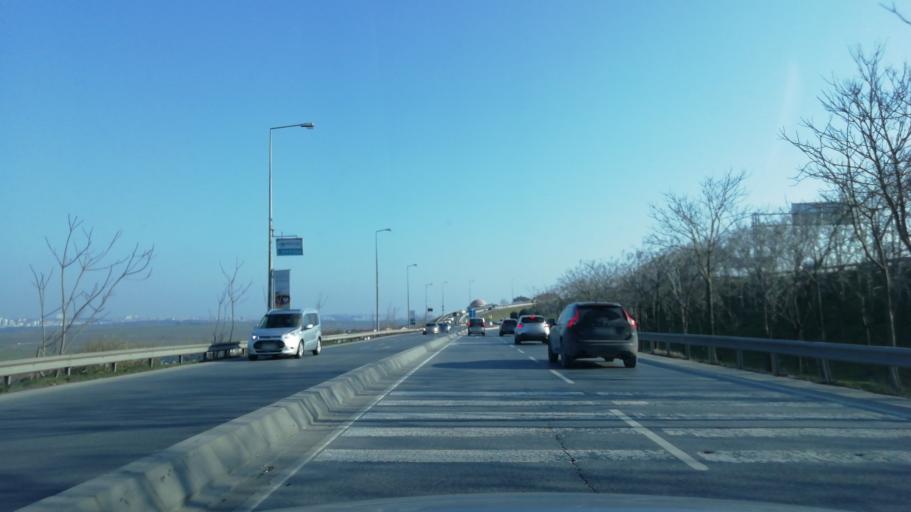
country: TR
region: Istanbul
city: Esenyurt
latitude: 41.0491
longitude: 28.6888
